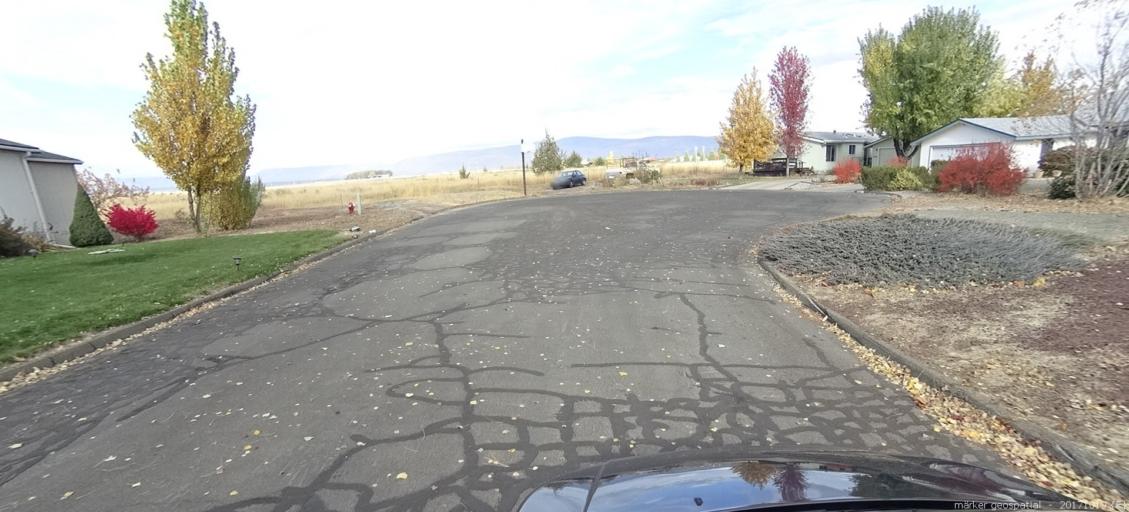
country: US
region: California
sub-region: Shasta County
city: Burney
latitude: 41.0287
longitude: -121.4245
